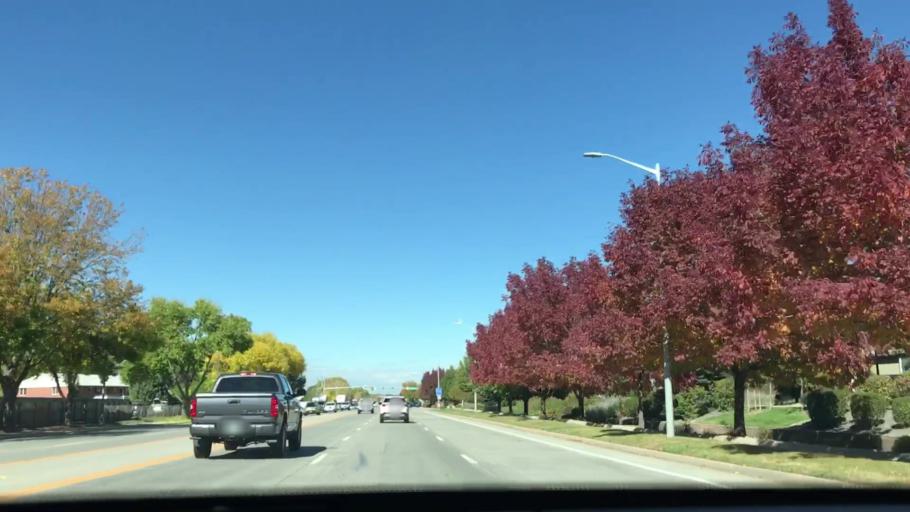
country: US
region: Colorado
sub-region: Boulder County
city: Longmont
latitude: 40.1424
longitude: -105.1024
